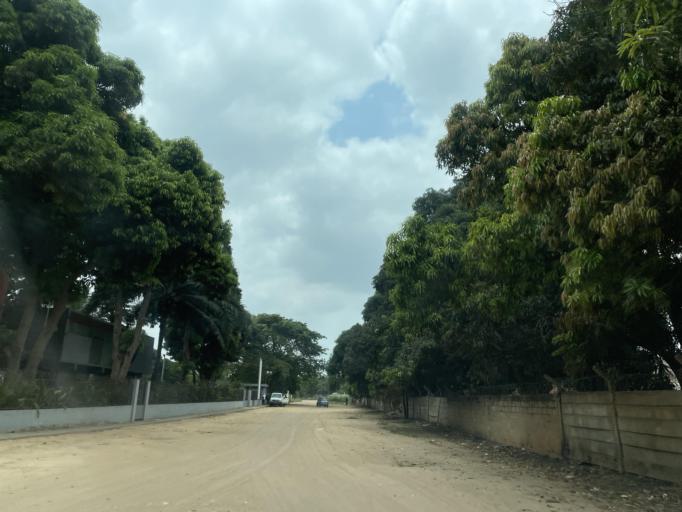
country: AO
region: Luanda
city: Luanda
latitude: -8.9119
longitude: 13.3768
